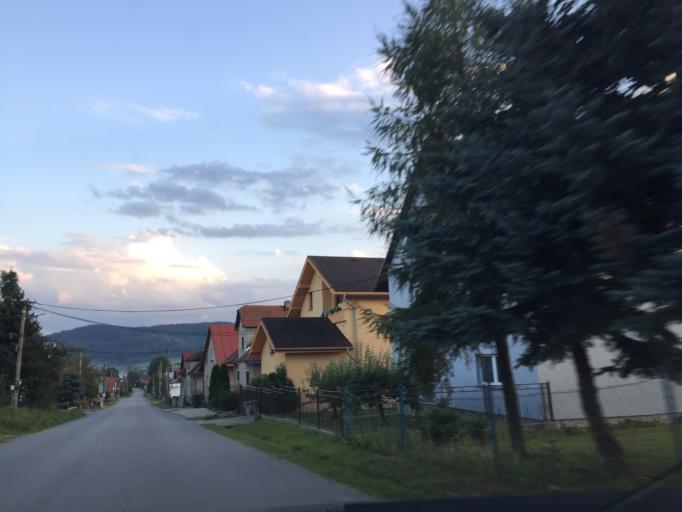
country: PL
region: Silesian Voivodeship
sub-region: Powiat zywiecki
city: Korbielow
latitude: 49.4663
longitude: 19.3831
